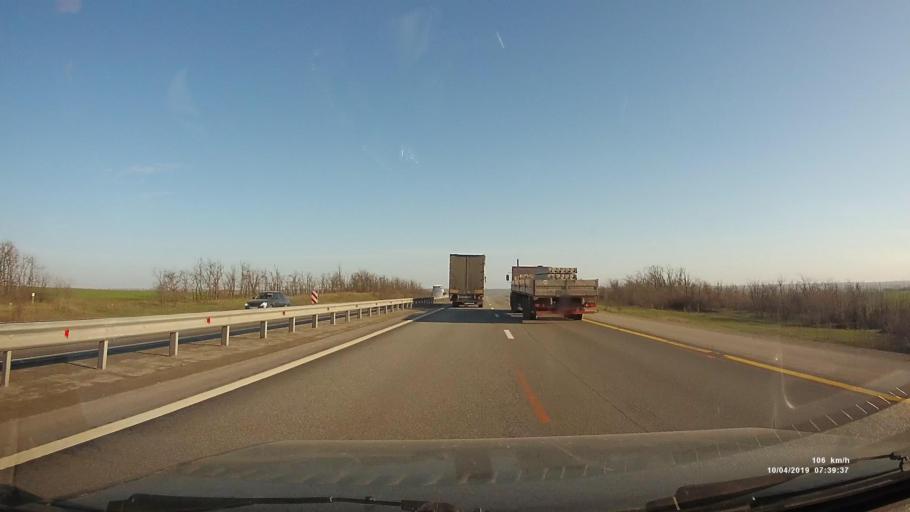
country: RU
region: Rostov
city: Likhoy
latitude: 48.1068
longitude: 40.2598
